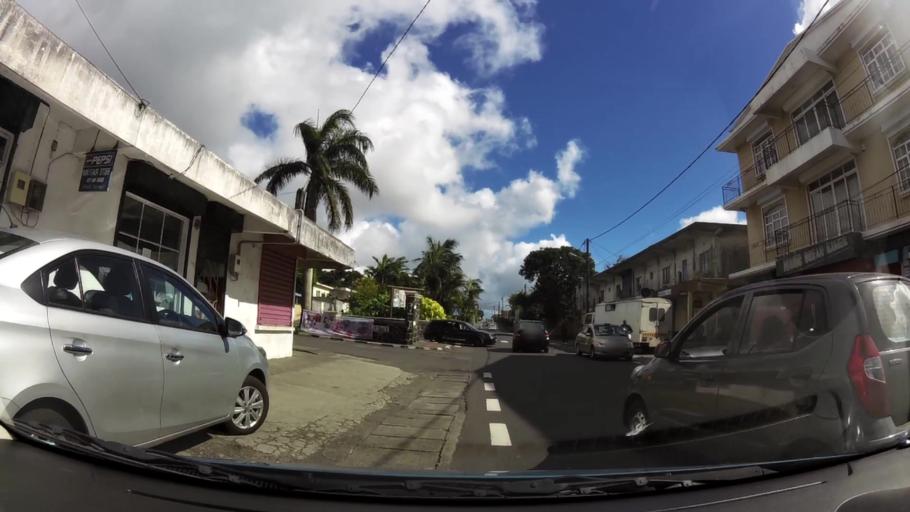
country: MU
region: Plaines Wilhems
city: Curepipe
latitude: -20.3305
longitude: 57.5249
